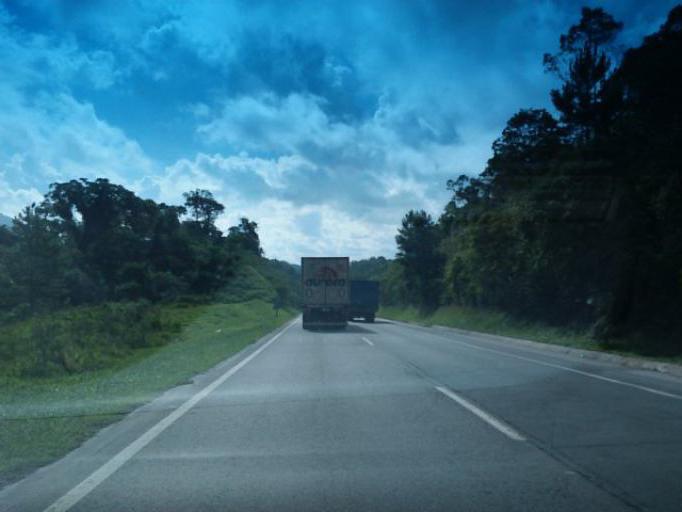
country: BR
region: Parana
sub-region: Antonina
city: Antonina
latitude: -25.1079
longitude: -48.7753
